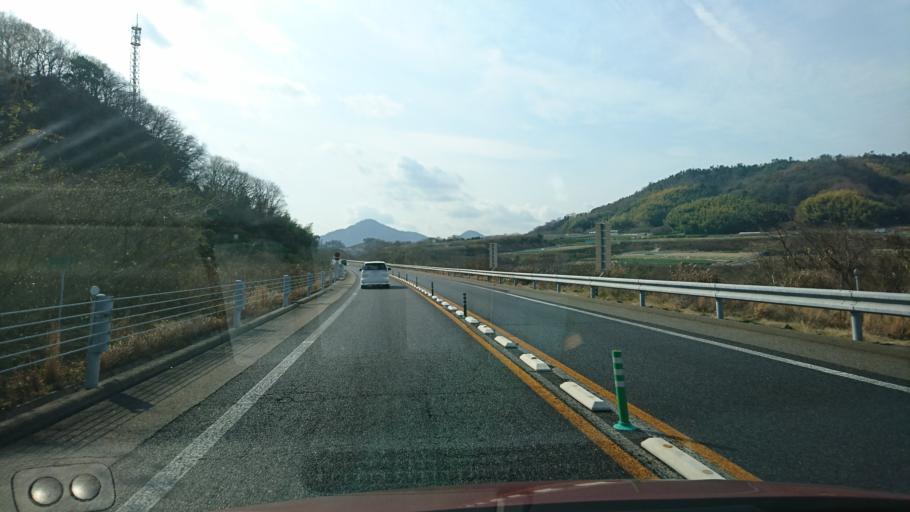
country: JP
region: Hiroshima
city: Innoshima
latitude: 34.3340
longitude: 133.1567
